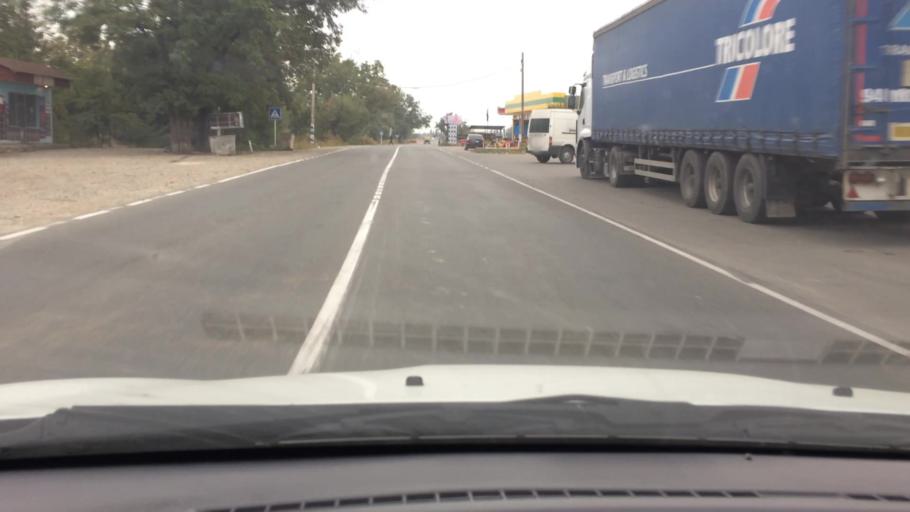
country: GE
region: Kvemo Kartli
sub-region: Marneuli
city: Marneuli
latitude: 41.3994
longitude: 44.8244
